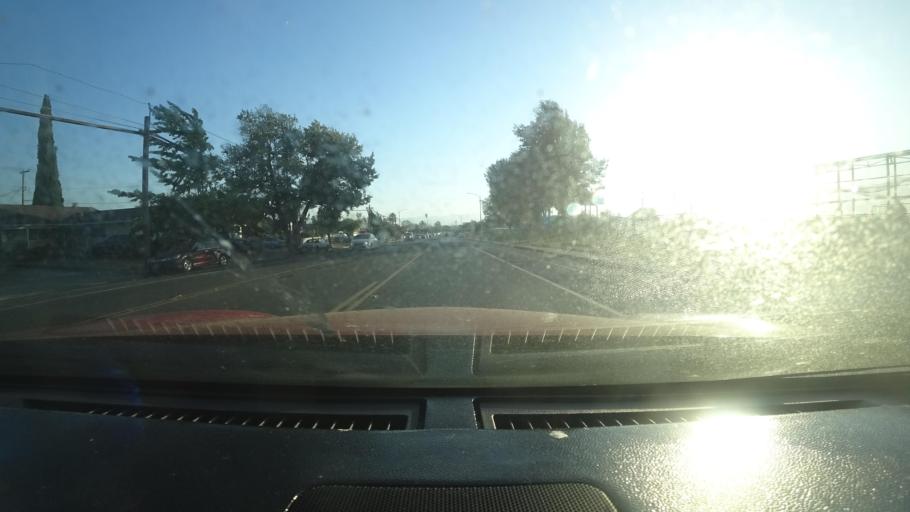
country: US
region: California
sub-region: Santa Clara County
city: Alum Rock
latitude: 37.3473
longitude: -121.8035
